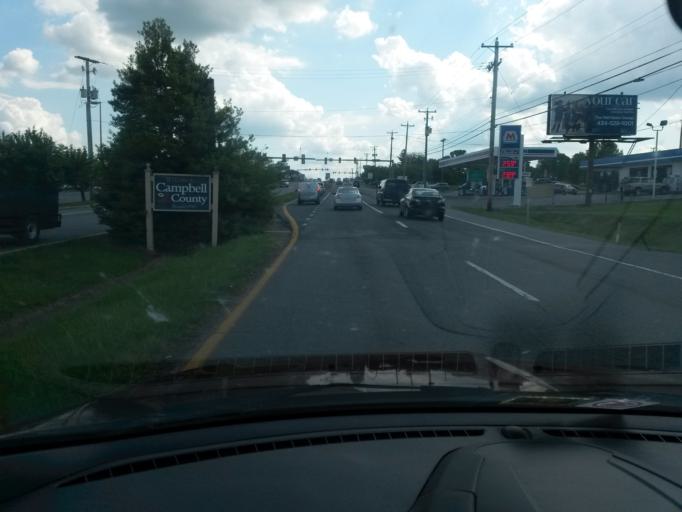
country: US
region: Virginia
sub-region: Campbell County
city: Timberlake
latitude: 37.3472
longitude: -79.2329
